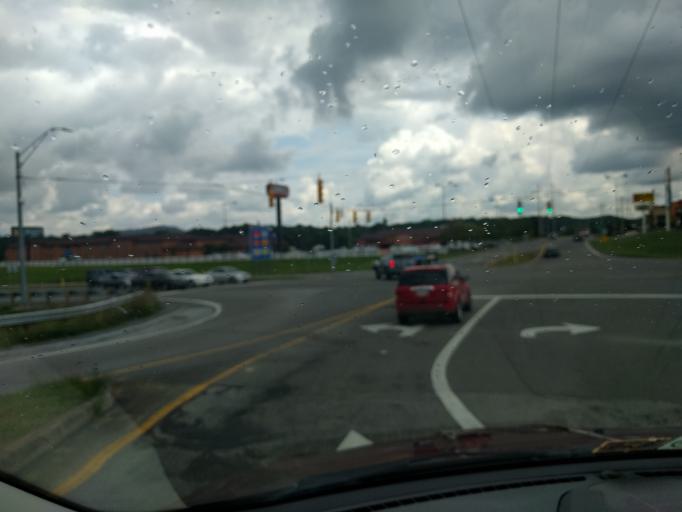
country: US
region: West Virginia
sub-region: Nicholas County
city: Summersville
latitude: 38.3061
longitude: -80.8343
